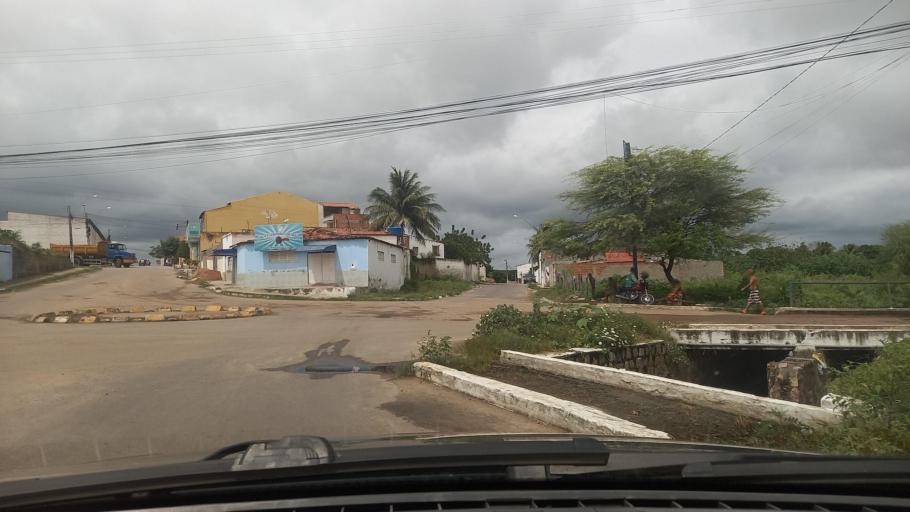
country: BR
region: Alagoas
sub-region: Delmiro Gouveia
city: Delmiro Gouveia
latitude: -9.3898
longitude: -38.0008
